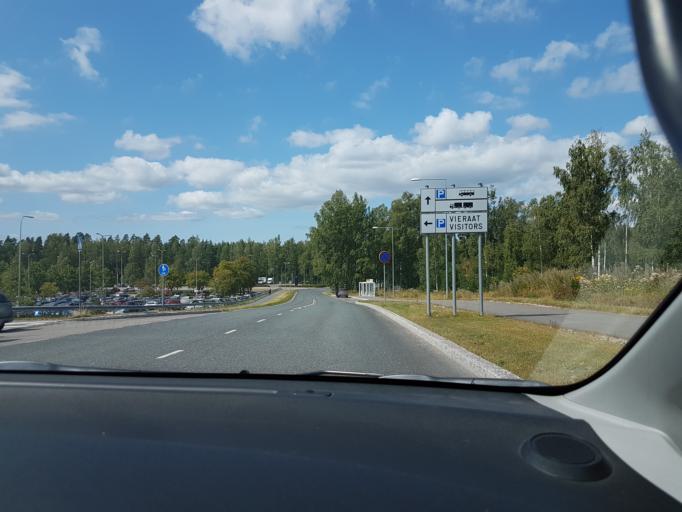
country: FI
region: Uusimaa
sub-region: Helsinki
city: Vantaa
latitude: 60.2578
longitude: 25.1048
